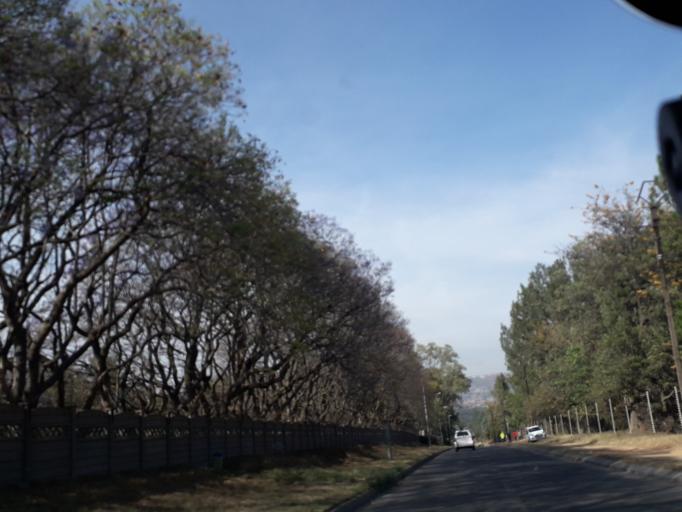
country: ZA
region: Gauteng
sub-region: West Rand District Municipality
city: Muldersdriseloop
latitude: -26.0681
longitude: 27.9006
